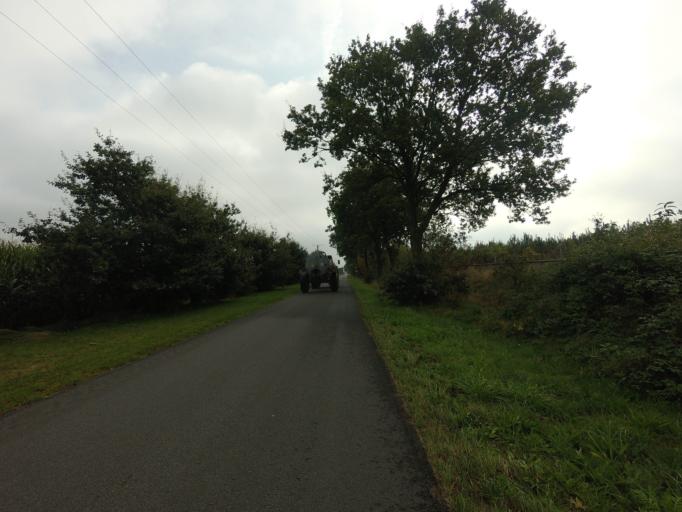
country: DE
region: Lower Saxony
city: Wielen
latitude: 52.5103
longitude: 6.7313
